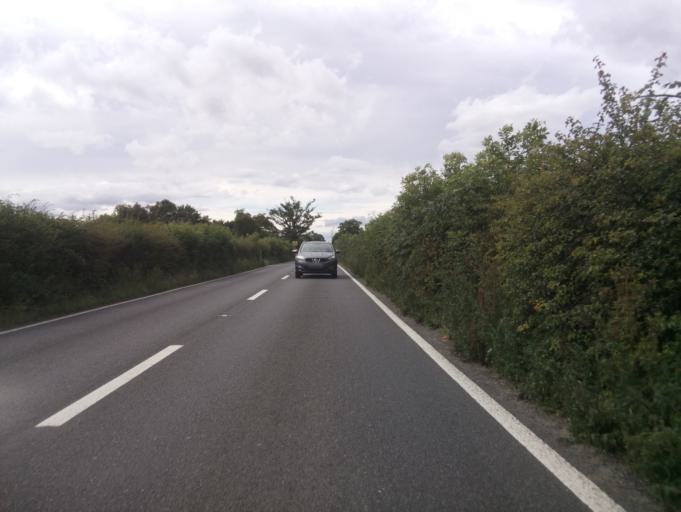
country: GB
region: England
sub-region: Somerset
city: Ilchester
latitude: 50.9710
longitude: -2.6671
